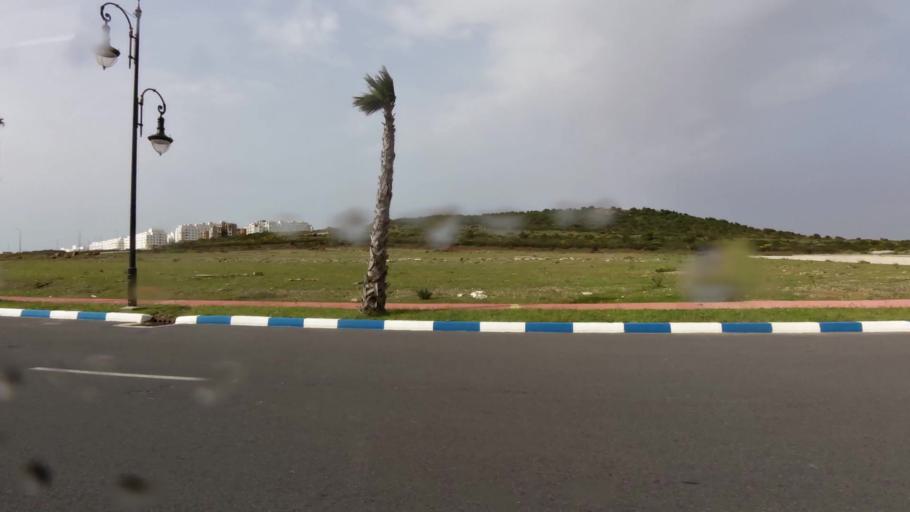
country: MA
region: Tanger-Tetouan
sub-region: Tanger-Assilah
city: Boukhalef
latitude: 35.6975
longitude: -5.9278
